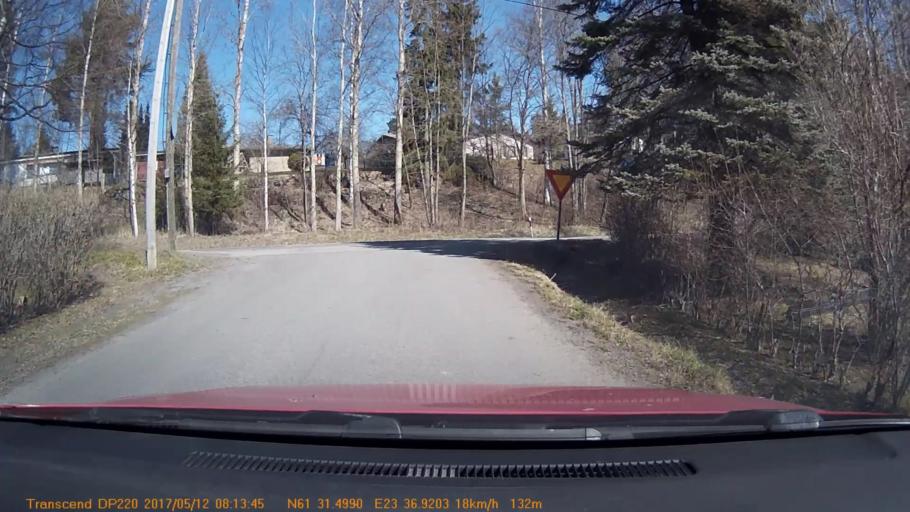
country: FI
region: Pirkanmaa
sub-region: Tampere
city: Yloejaervi
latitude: 61.5249
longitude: 23.6154
